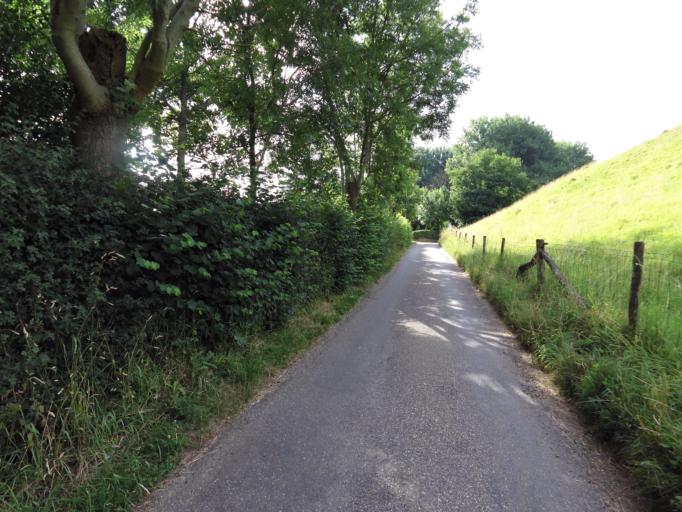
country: NL
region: Limburg
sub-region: Valkenburg aan de Geul
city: Schin op Geul
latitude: 50.8408
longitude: 5.8788
